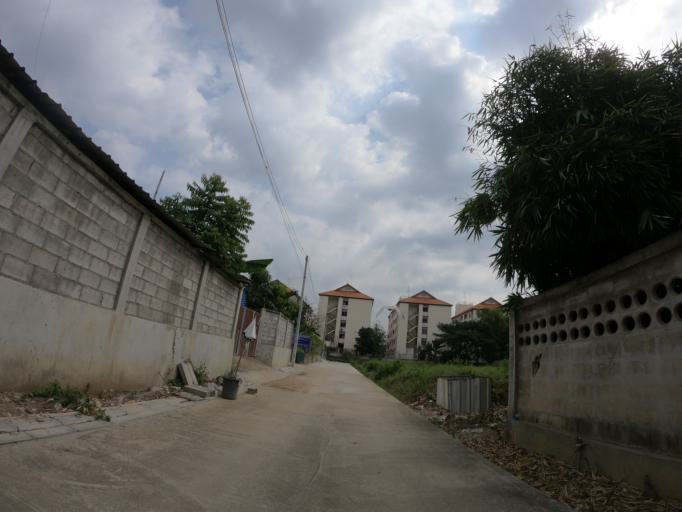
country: TH
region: Chiang Mai
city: Chiang Mai
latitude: 18.7580
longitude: 98.9846
